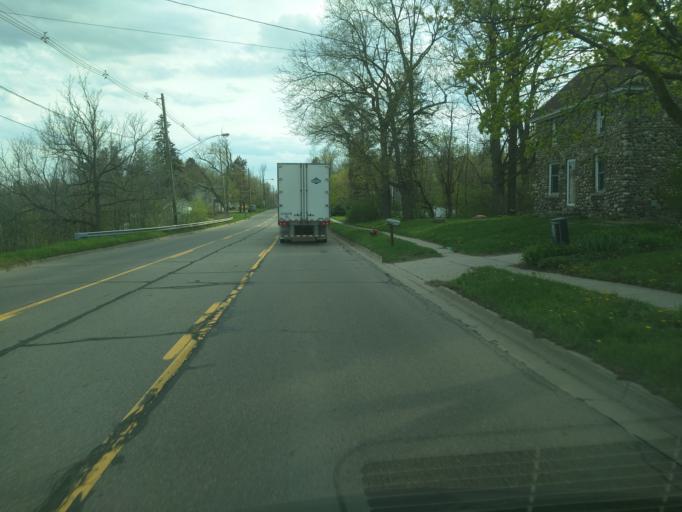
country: US
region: Michigan
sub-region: Eaton County
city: Eaton Rapids
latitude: 42.5227
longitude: -84.6495
